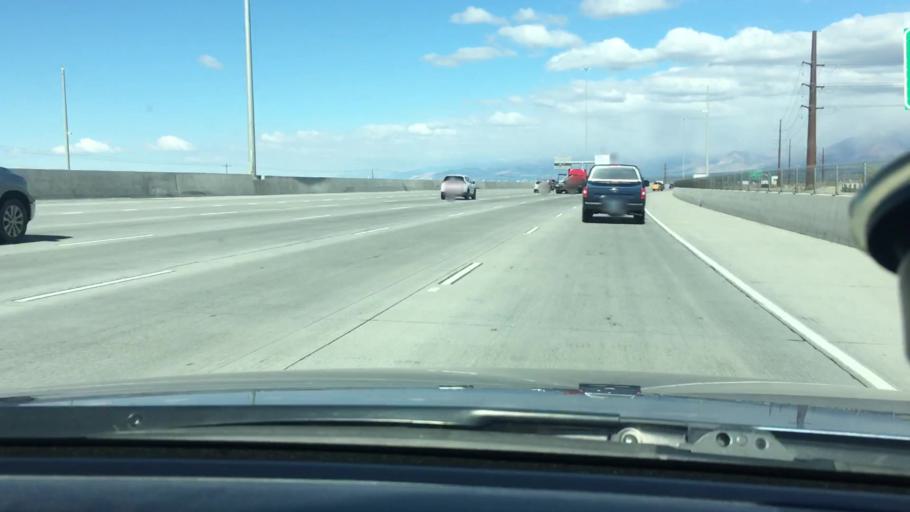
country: US
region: Utah
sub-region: Salt Lake County
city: Bluffdale
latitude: 40.4623
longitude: -111.9138
